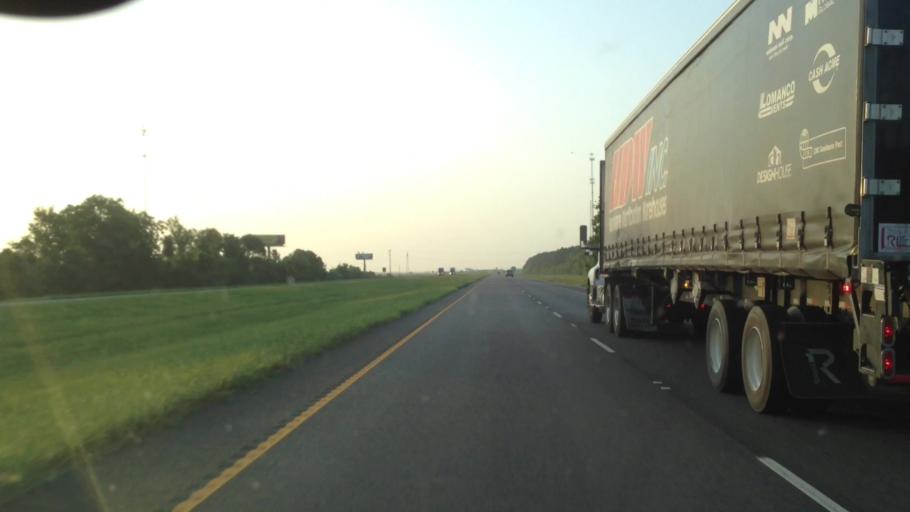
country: US
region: Louisiana
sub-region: Red River Parish
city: Coushatta
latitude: 31.8456
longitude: -93.2928
